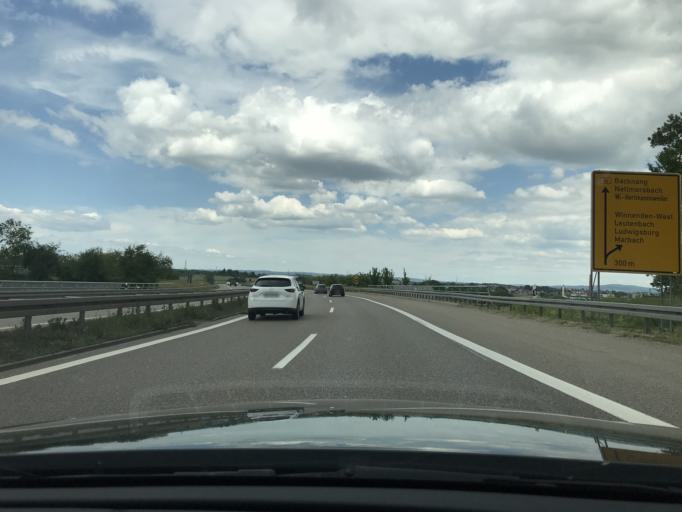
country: DE
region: Baden-Wuerttemberg
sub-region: Regierungsbezirk Stuttgart
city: Winnenden
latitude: 48.8745
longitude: 9.3817
